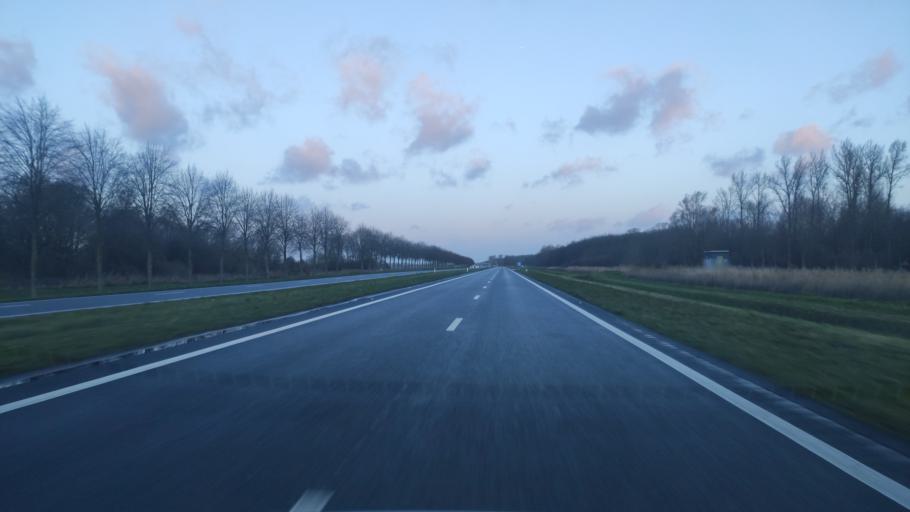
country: NL
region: Flevoland
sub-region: Gemeente Zeewolde
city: Zeewolde
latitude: 52.4353
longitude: 5.5642
